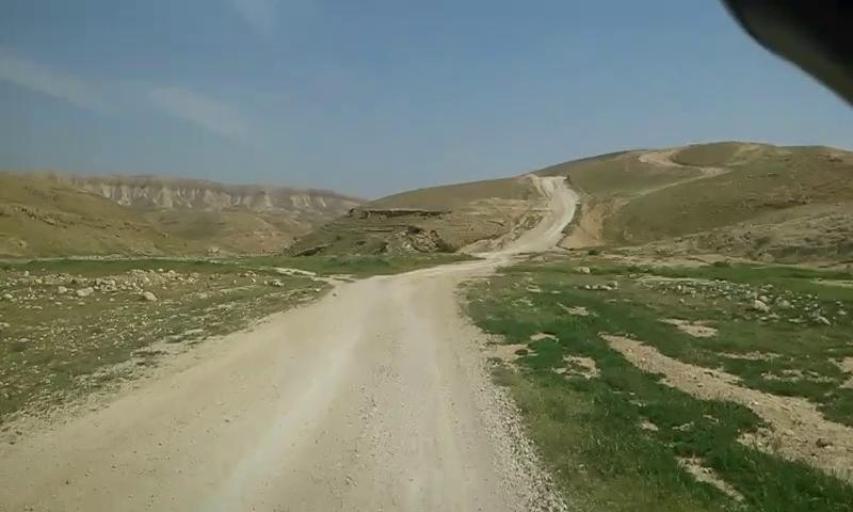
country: PS
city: `Arab ar Rashaydah
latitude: 31.5040
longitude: 35.2924
